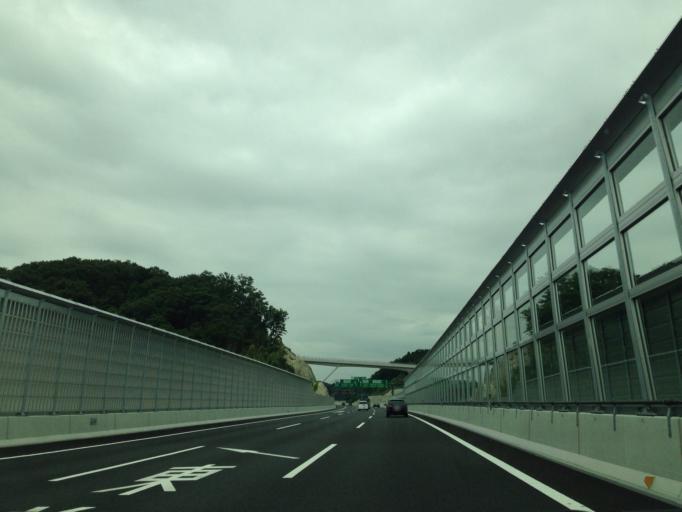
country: JP
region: Aichi
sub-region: Toyota-shi
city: Toyota
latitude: 35.0397
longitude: 137.2114
